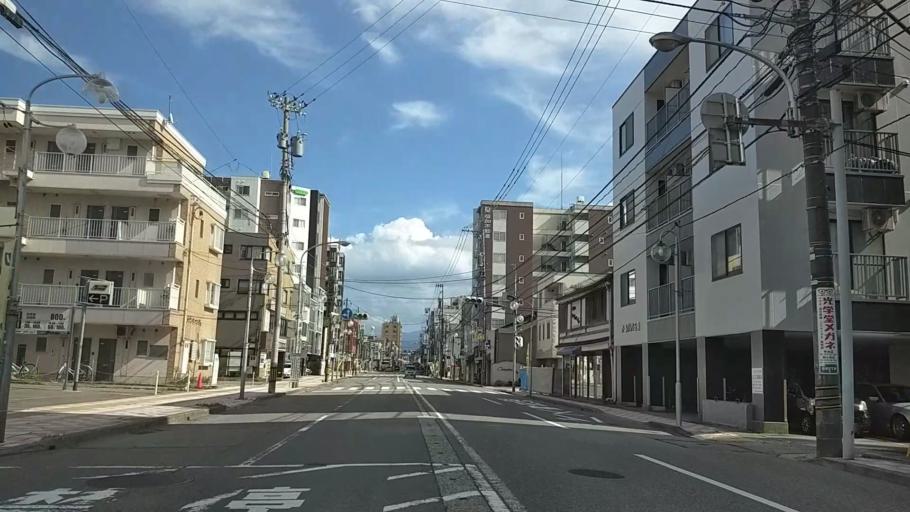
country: JP
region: Ishikawa
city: Nonoichi
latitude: 36.5561
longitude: 136.6696
